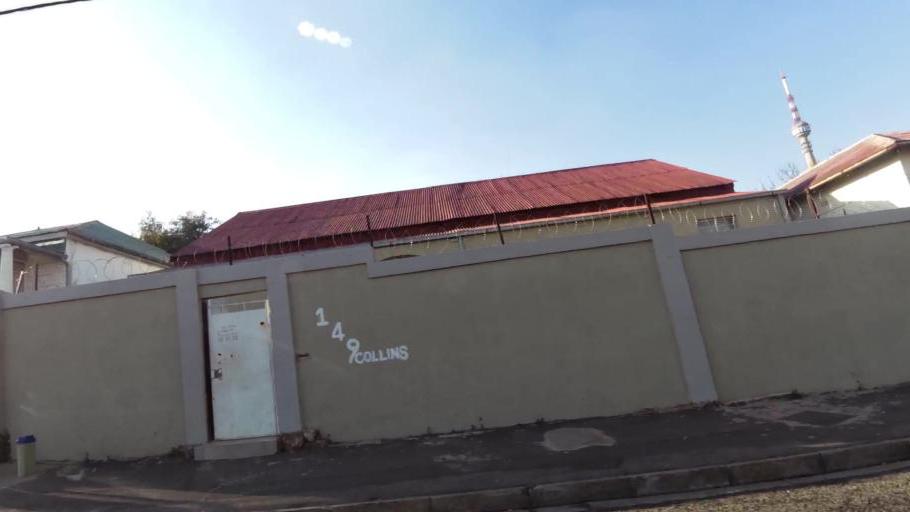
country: ZA
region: Gauteng
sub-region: City of Johannesburg Metropolitan Municipality
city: Johannesburg
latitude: -26.1945
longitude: 28.0017
